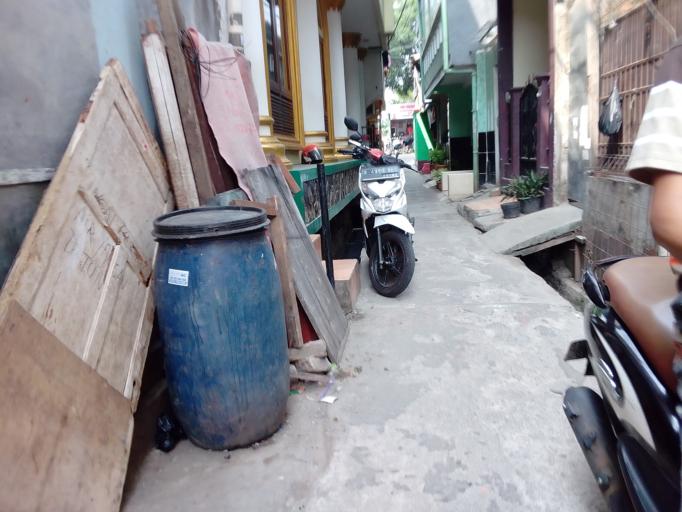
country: ID
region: Jakarta Raya
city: Jakarta
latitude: -6.1906
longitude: 106.8090
